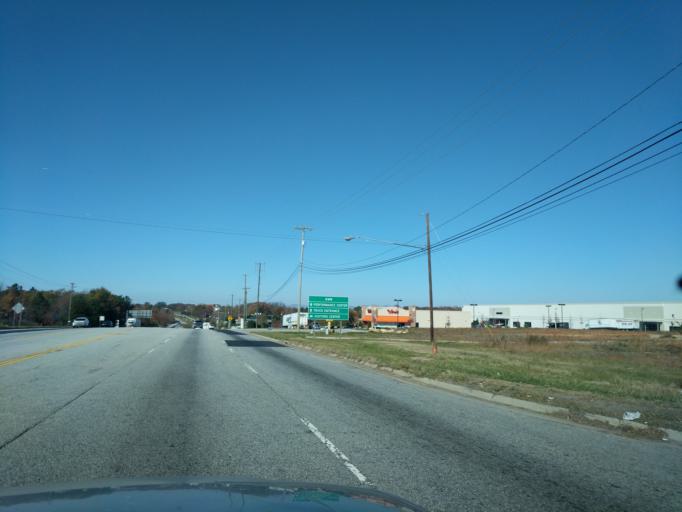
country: US
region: South Carolina
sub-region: Spartanburg County
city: Duncan
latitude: 34.8954
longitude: -82.1631
